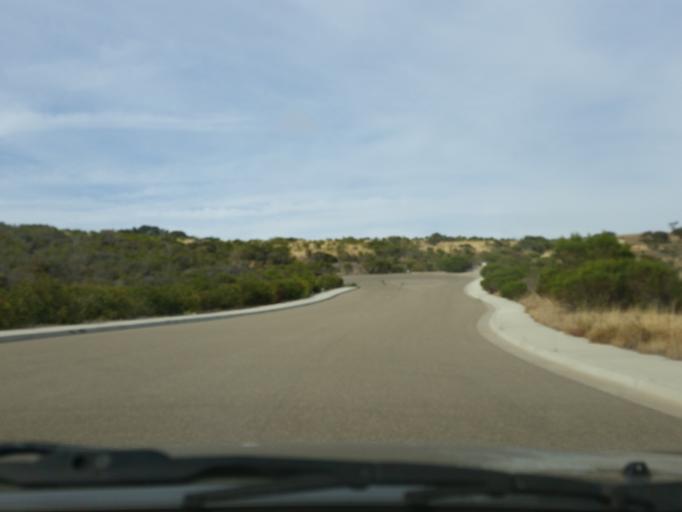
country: US
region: California
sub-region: San Luis Obispo County
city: Pismo Beach
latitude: 35.1466
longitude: -120.6302
